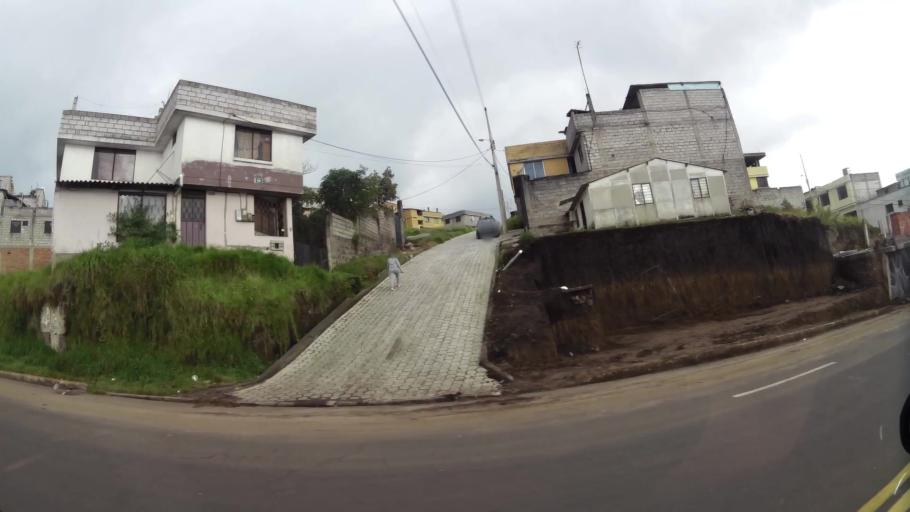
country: EC
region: Pichincha
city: Sangolqui
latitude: -0.3078
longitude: -78.5232
